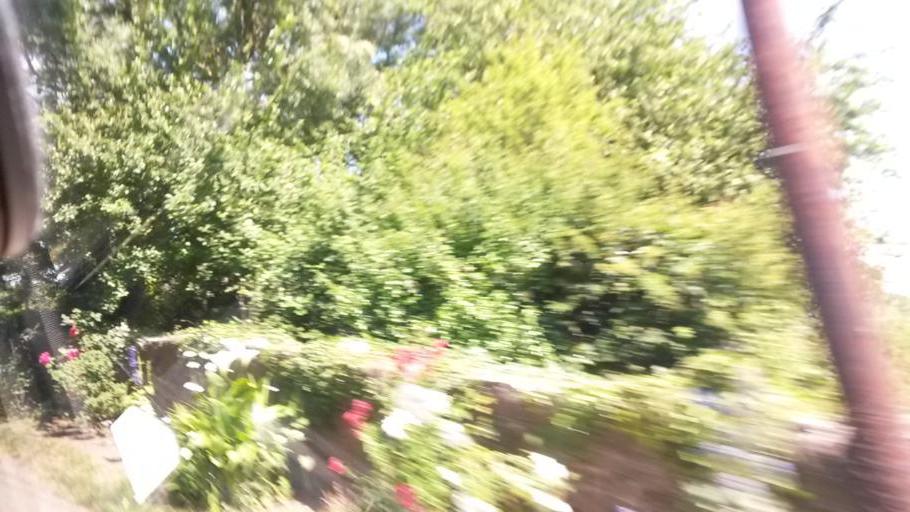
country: IE
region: Leinster
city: Balrothery
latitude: 53.5377
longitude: -6.2479
